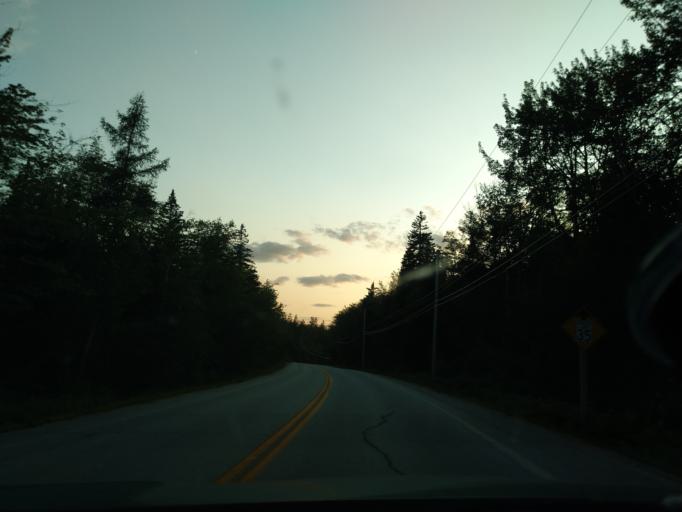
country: US
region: Maine
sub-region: Hancock County
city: Gouldsboro
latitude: 44.3940
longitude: -68.0666
